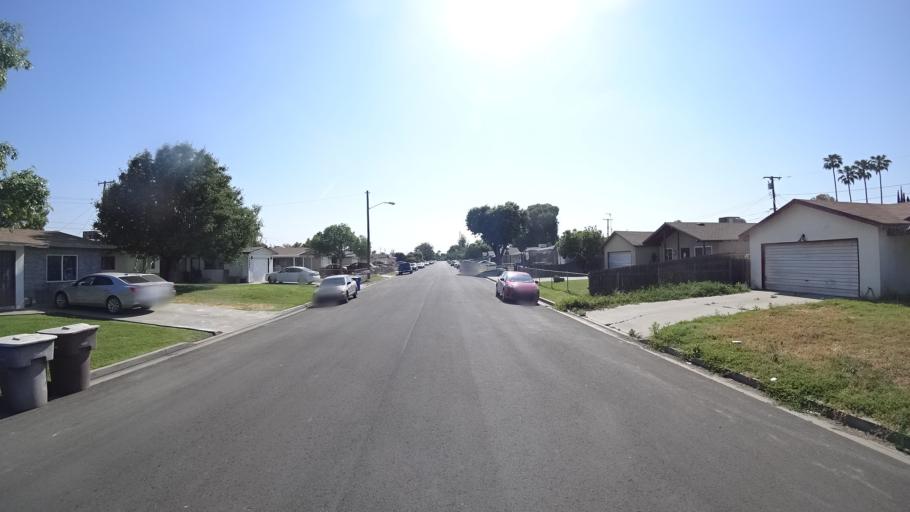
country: US
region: California
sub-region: Kings County
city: Home Garden
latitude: 36.3003
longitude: -119.6406
